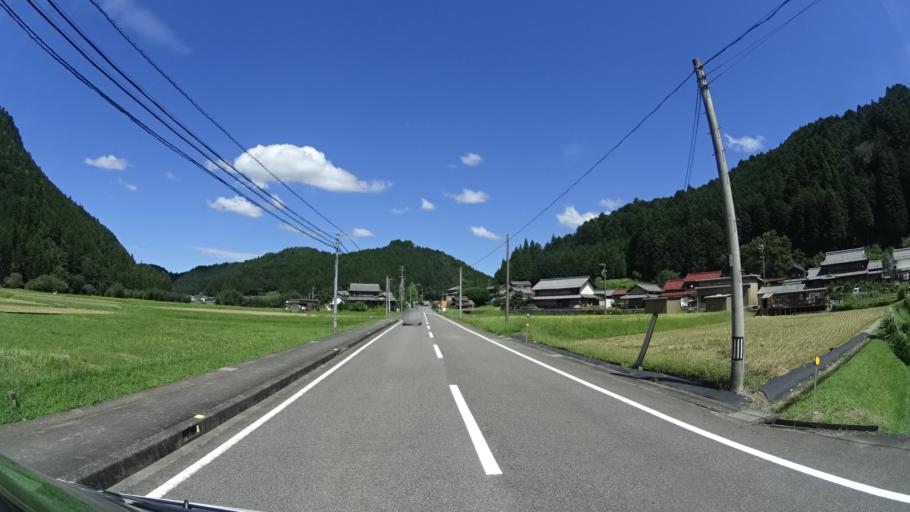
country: JP
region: Gifu
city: Minokamo
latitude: 35.5693
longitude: 137.0838
